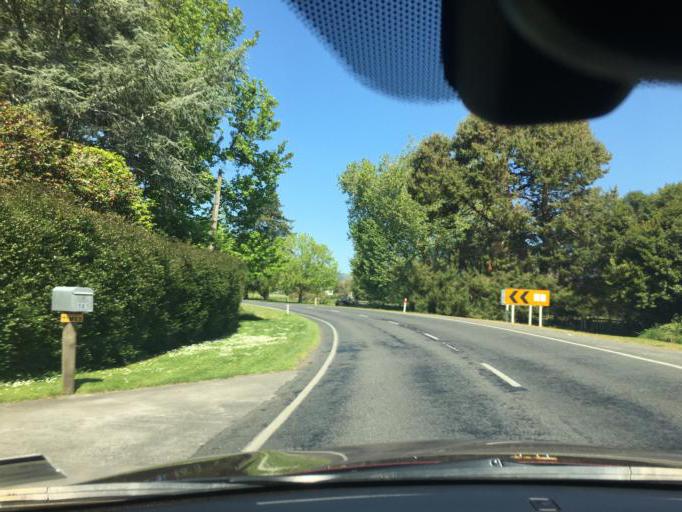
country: NZ
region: Waikato
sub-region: Waipa District
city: Cambridge
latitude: -37.9148
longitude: 175.4600
